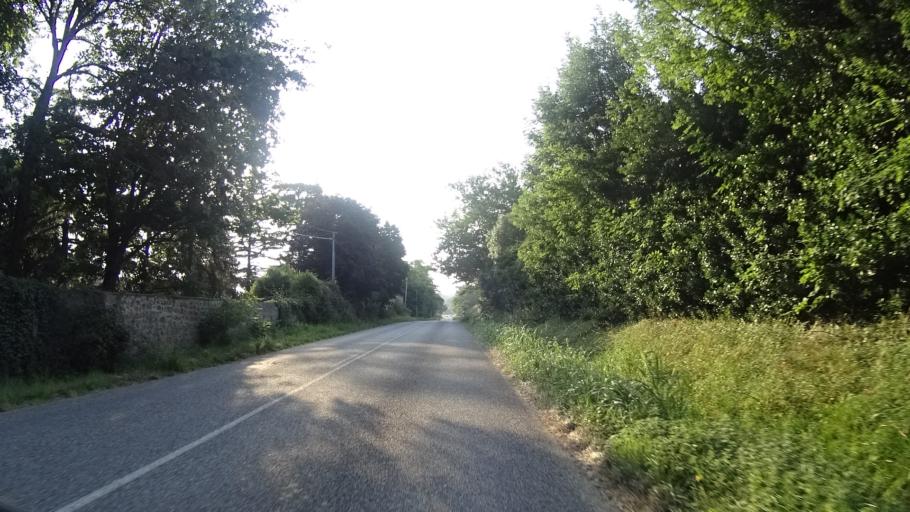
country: FR
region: Midi-Pyrenees
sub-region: Departement de l'Ariege
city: Mirepoix
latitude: 43.0843
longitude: 1.8984
